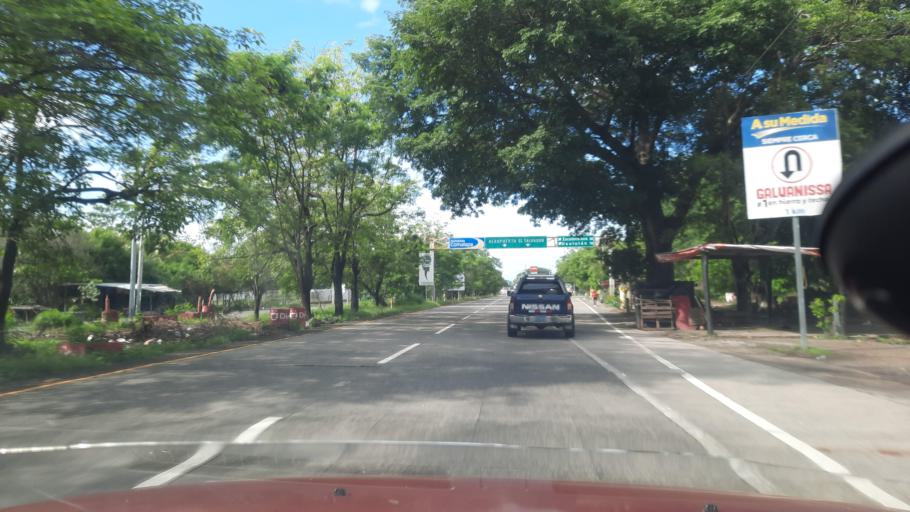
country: SV
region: La Paz
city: El Rosario
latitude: 13.4857
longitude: -89.0665
